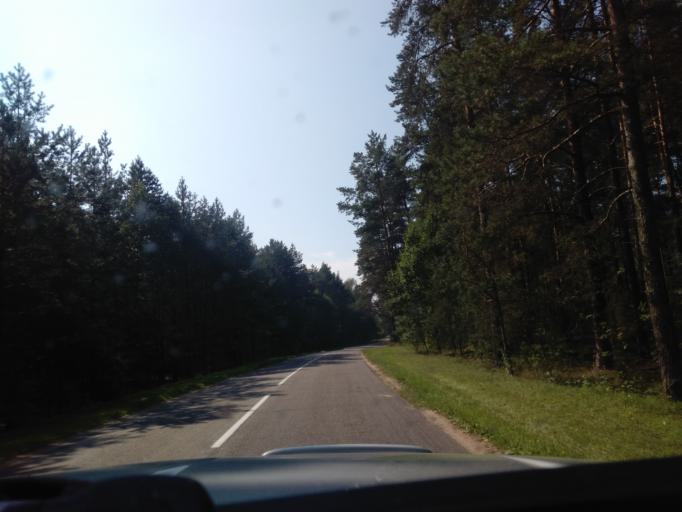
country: BY
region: Minsk
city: Valozhyn
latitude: 54.0222
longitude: 26.6034
